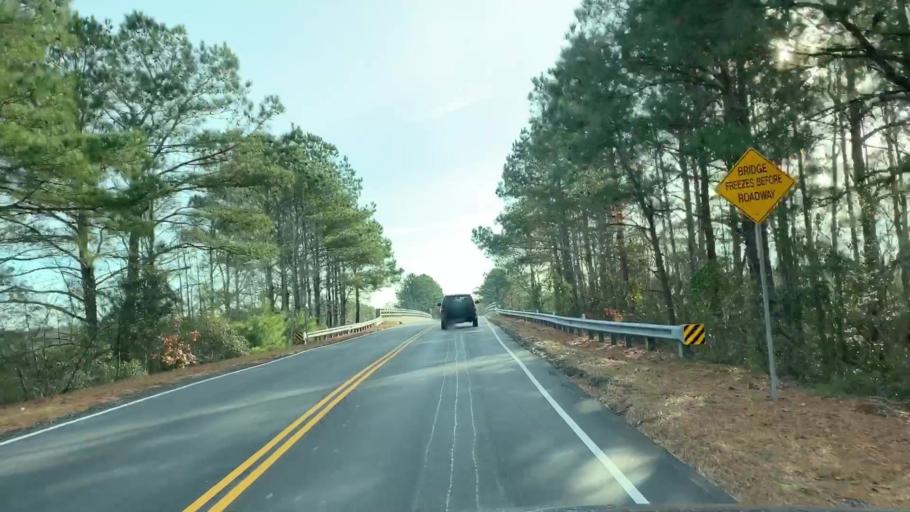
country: US
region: Virginia
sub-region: City of Virginia Beach
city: Virginia Beach
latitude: 36.6956
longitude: -76.0421
